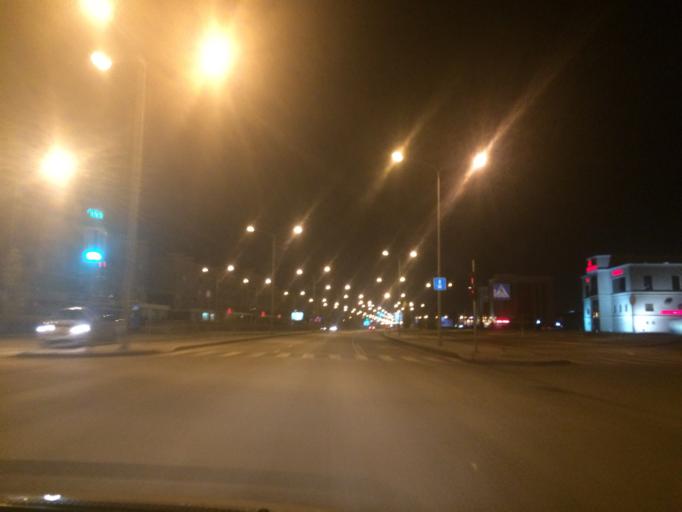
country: KZ
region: Astana Qalasy
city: Astana
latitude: 51.1485
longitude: 71.3886
